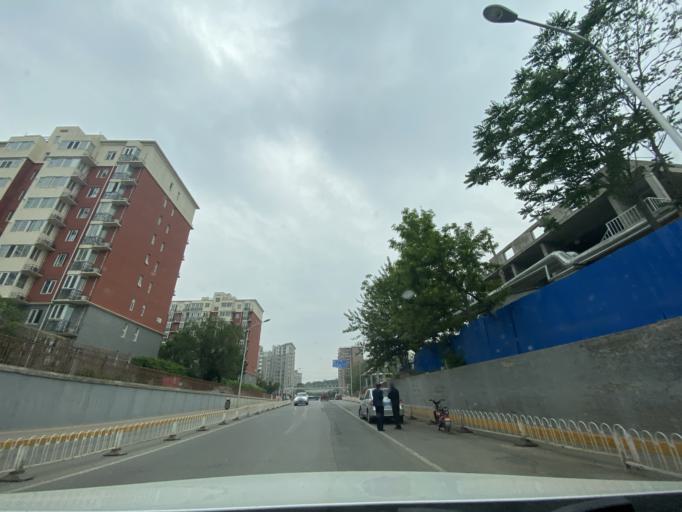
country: CN
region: Beijing
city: Sijiqing
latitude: 39.9301
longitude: 116.2421
